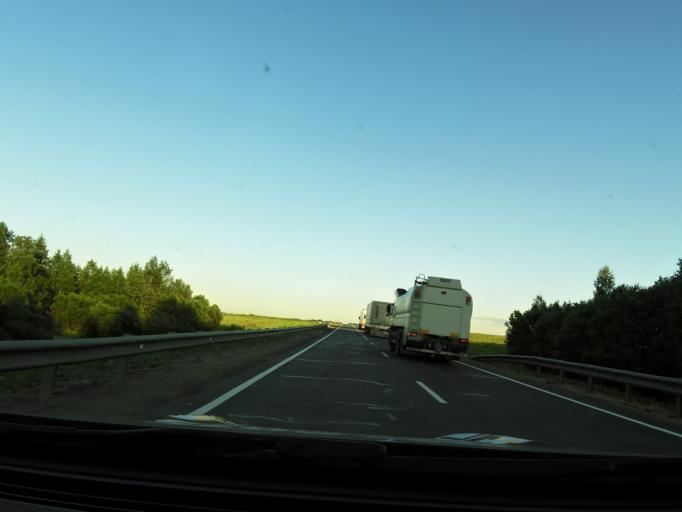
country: RU
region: Vologda
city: Gryazovets
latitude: 58.8315
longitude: 40.2134
